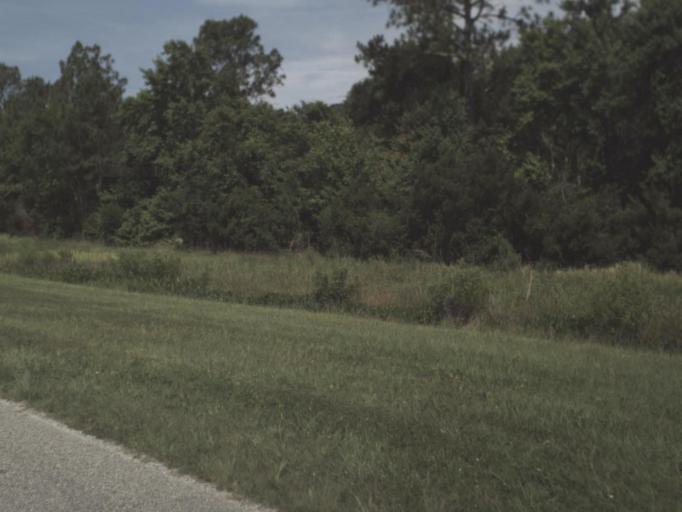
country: US
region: Florida
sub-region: Putnam County
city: East Palatka
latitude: 29.6939
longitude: -81.5633
